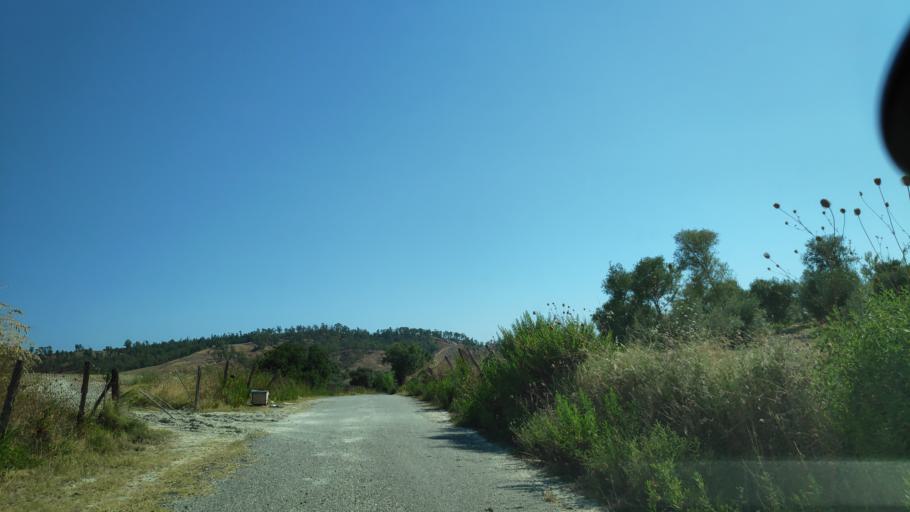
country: IT
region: Calabria
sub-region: Provincia di Reggio Calabria
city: Monasterace
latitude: 38.4321
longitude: 16.5249
